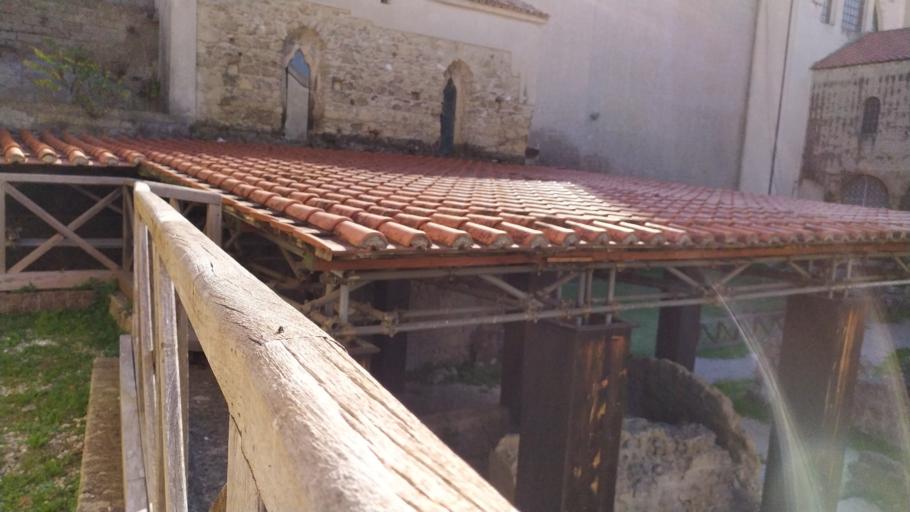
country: IT
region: Campania
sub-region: Provincia di Napoli
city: Cimitile
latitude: 40.9409
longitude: 14.5244
